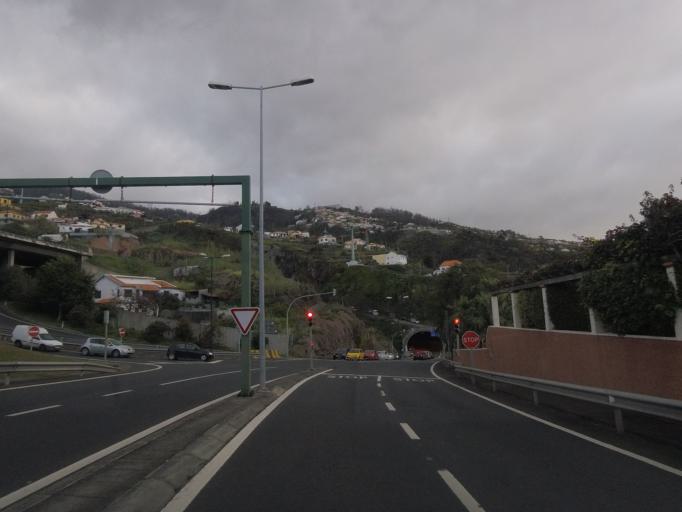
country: PT
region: Madeira
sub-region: Funchal
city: Nossa Senhora do Monte
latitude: 32.6618
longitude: -16.9035
